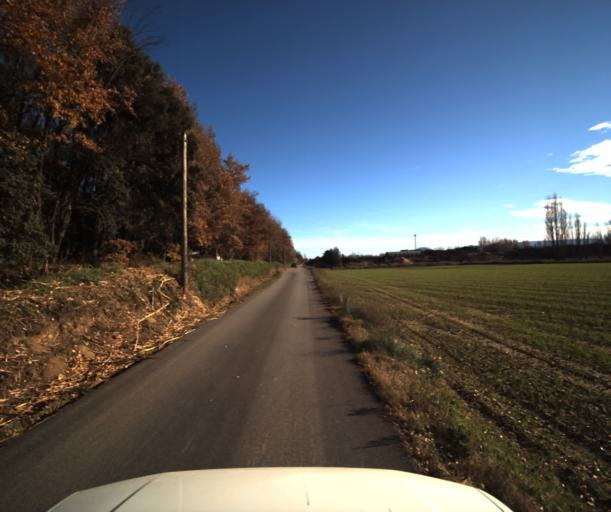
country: FR
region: Provence-Alpes-Cote d'Azur
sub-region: Departement du Vaucluse
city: Pertuis
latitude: 43.6968
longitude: 5.4740
